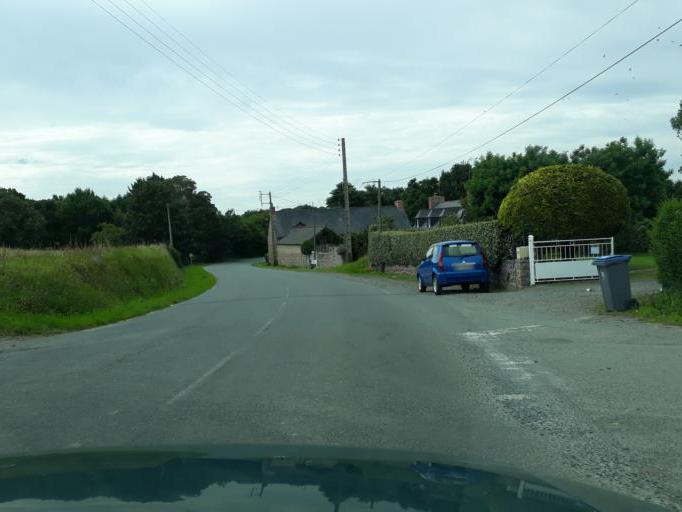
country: FR
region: Brittany
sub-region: Departement des Cotes-d'Armor
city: Paimpol
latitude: 48.7687
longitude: -3.0488
